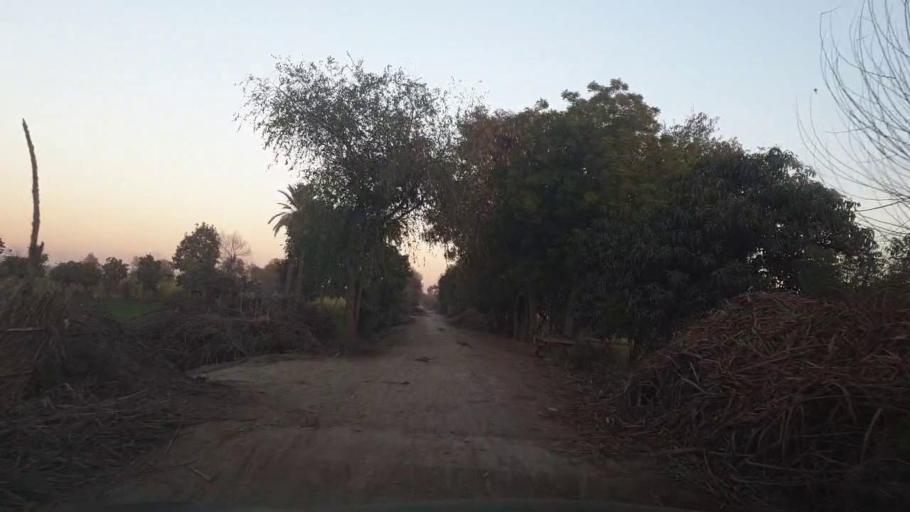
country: PK
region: Sindh
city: Ghotki
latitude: 28.0107
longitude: 69.3774
